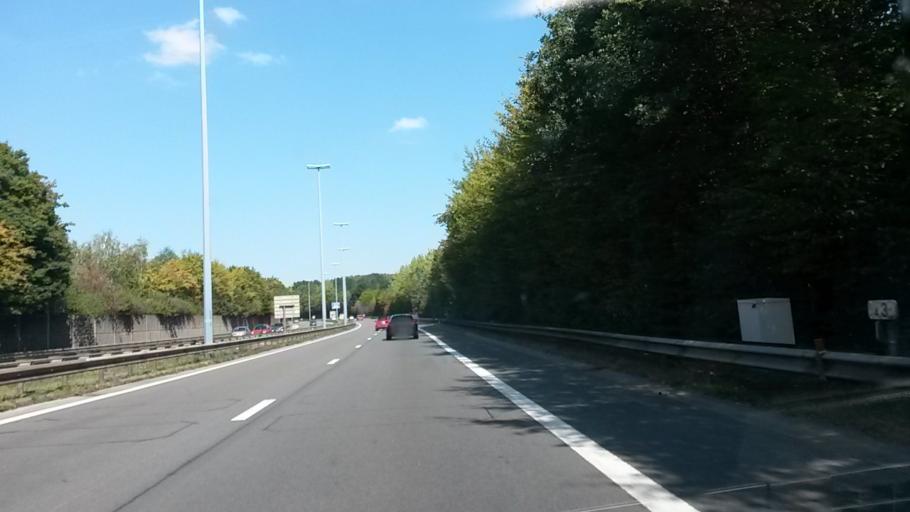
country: BE
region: Wallonia
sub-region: Province du Hainaut
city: Chatelet
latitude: 50.4332
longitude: 4.4986
